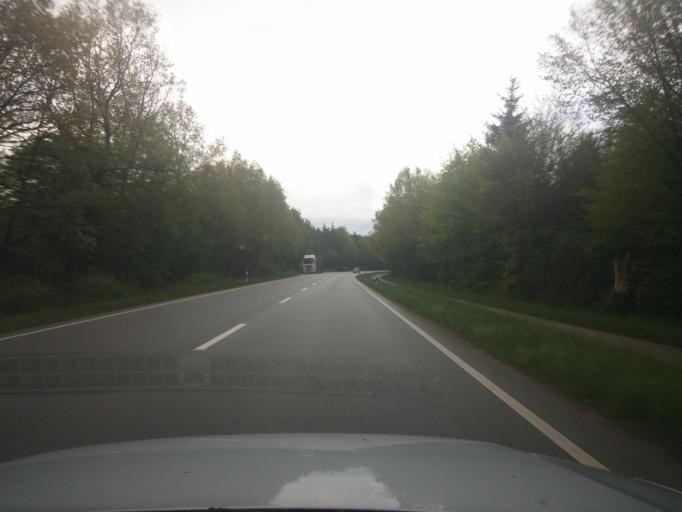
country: DE
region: Bavaria
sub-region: Upper Bavaria
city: Putzbrunn
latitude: 48.0897
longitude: 11.7216
